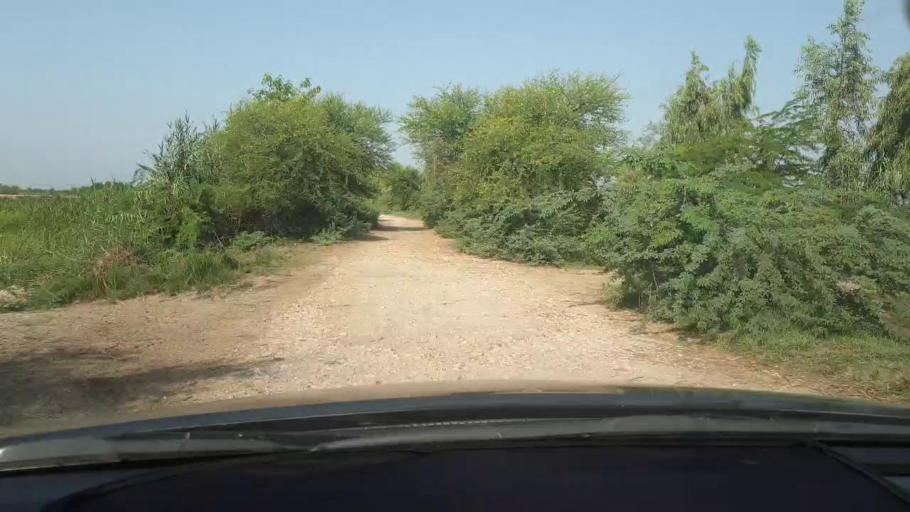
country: PK
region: Sindh
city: Tando Bago
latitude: 24.6835
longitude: 69.0800
